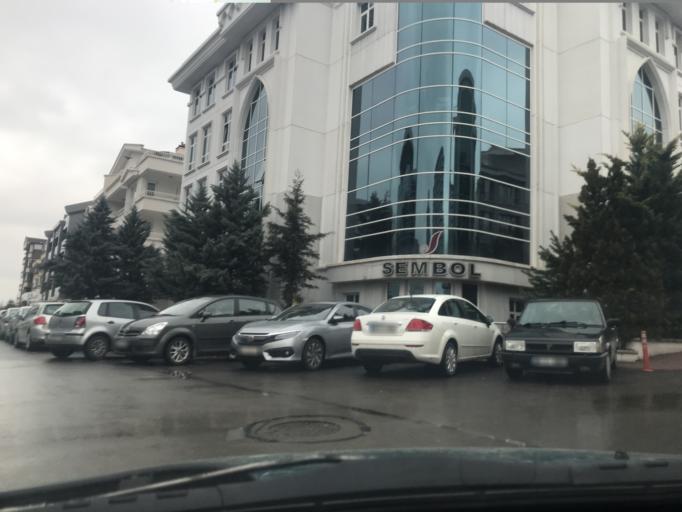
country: TR
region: Ankara
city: Batikent
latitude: 39.9108
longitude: 32.7657
